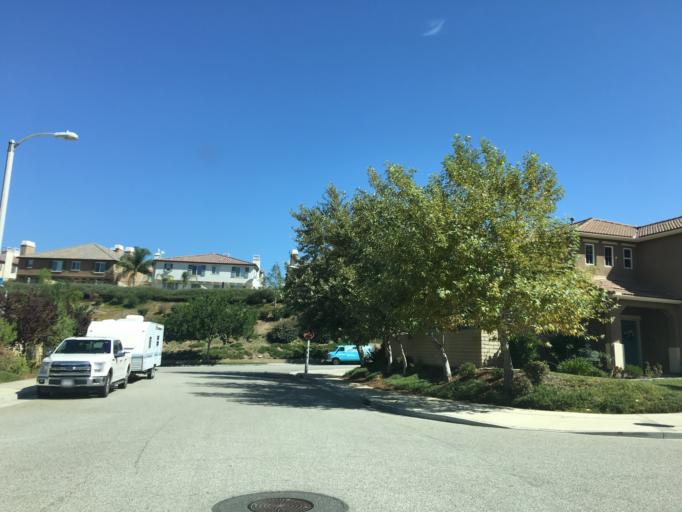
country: US
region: California
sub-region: Los Angeles County
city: Santa Clarita
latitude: 34.4428
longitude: -118.4759
